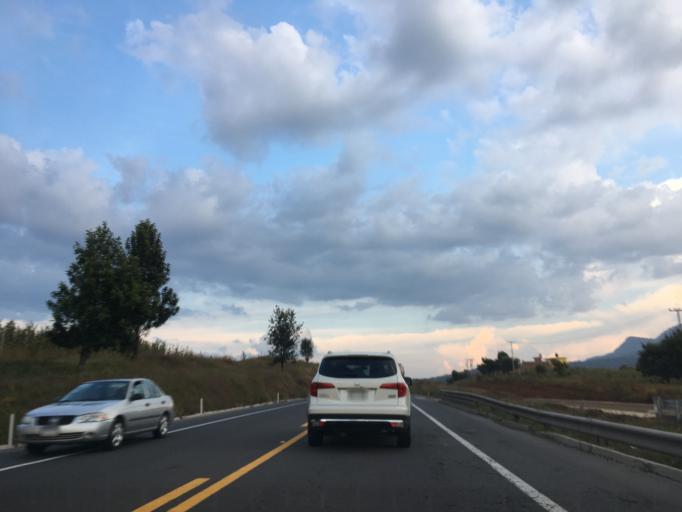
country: MX
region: Michoacan
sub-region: Patzcuaro
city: Colonia Vista Bella (Lomas del Peaje)
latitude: 19.5023
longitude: -101.5826
